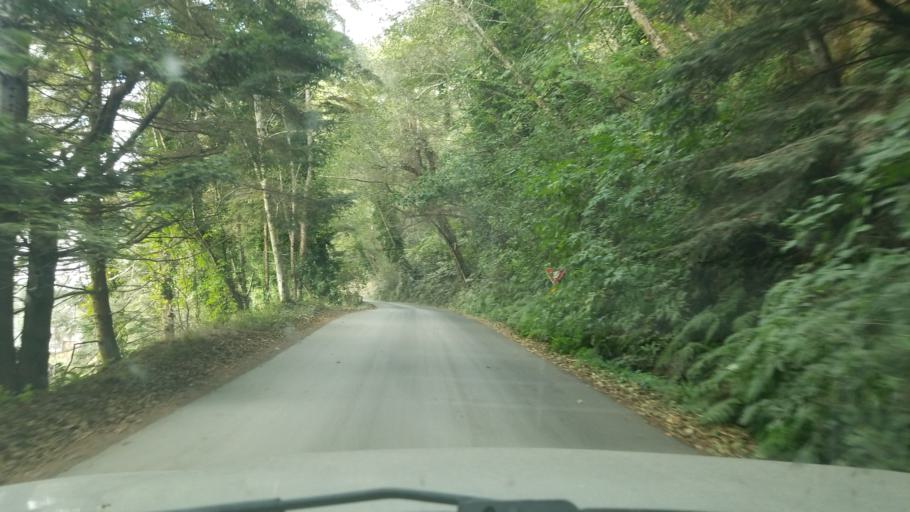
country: US
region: California
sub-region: Mendocino County
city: Fort Bragg
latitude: 39.4272
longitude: -123.7962
